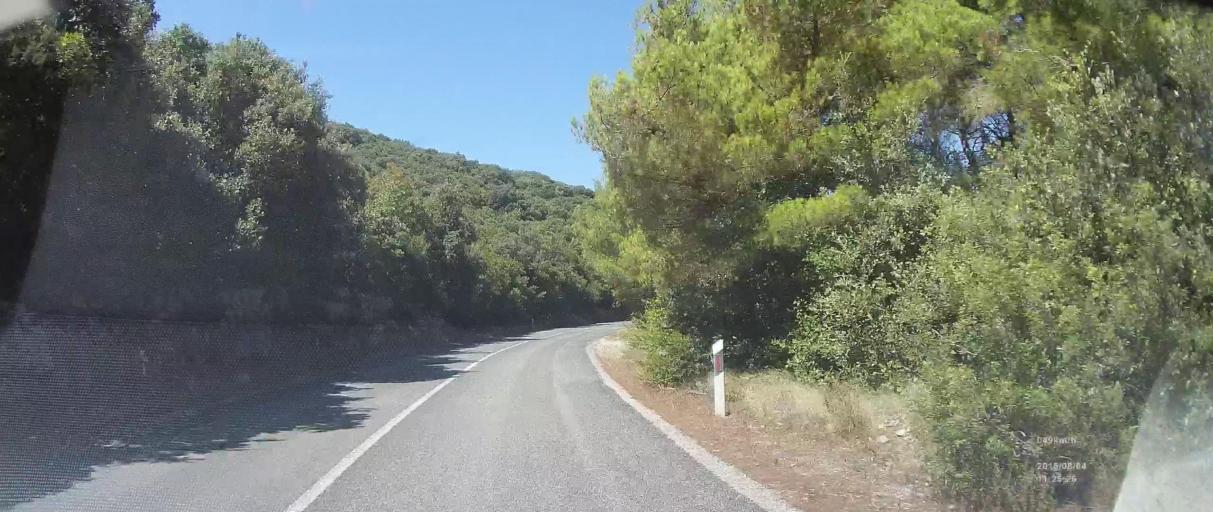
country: HR
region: Dubrovacko-Neretvanska
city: Blato
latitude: 42.7860
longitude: 17.3966
